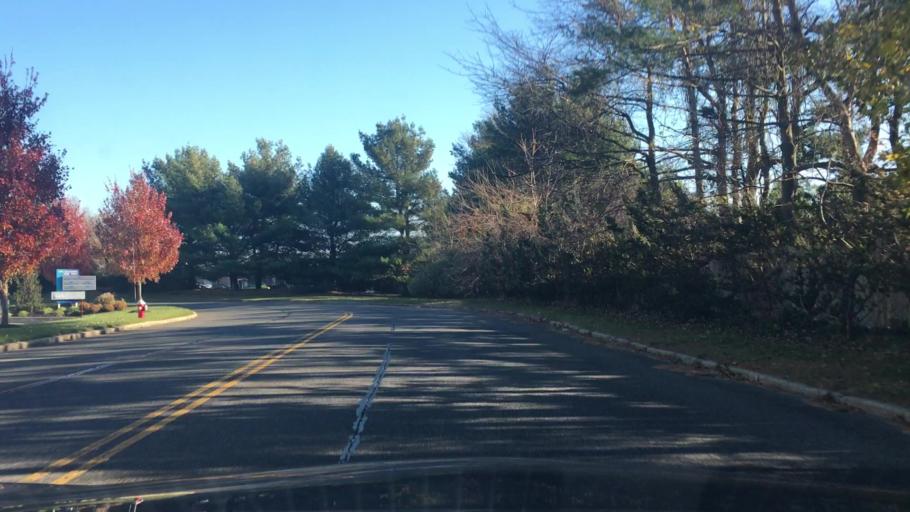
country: US
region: New York
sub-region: Nassau County
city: Syosset
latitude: 40.8038
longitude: -73.4876
